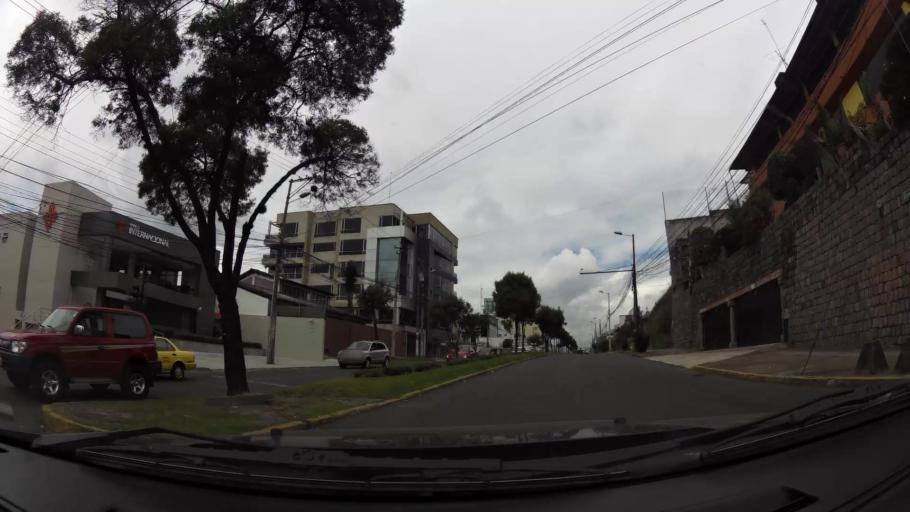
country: EC
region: Pichincha
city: Quito
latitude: -0.1657
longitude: -78.4893
